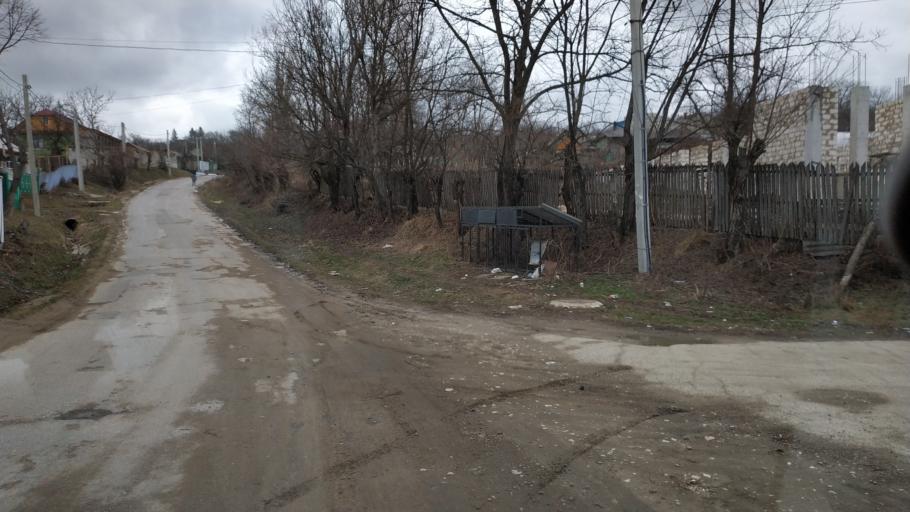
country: MD
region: Calarasi
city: Calarasi
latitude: 47.2050
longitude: 28.2502
